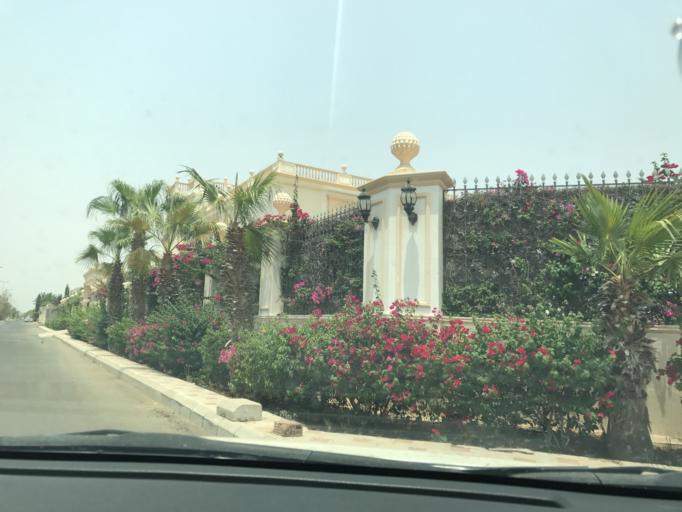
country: SA
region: Makkah
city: Jeddah
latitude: 21.6827
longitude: 39.1049
